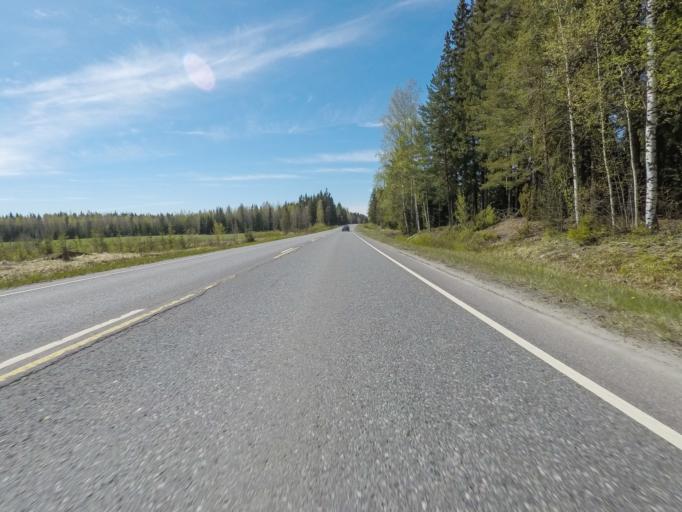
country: FI
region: Haeme
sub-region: Forssa
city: Humppila
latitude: 60.9653
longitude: 23.3907
